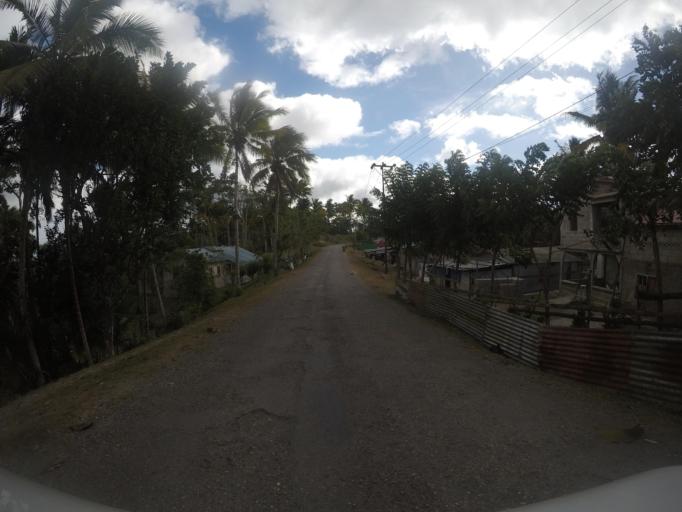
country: TL
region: Lautem
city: Lospalos
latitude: -8.5331
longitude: 126.9199
